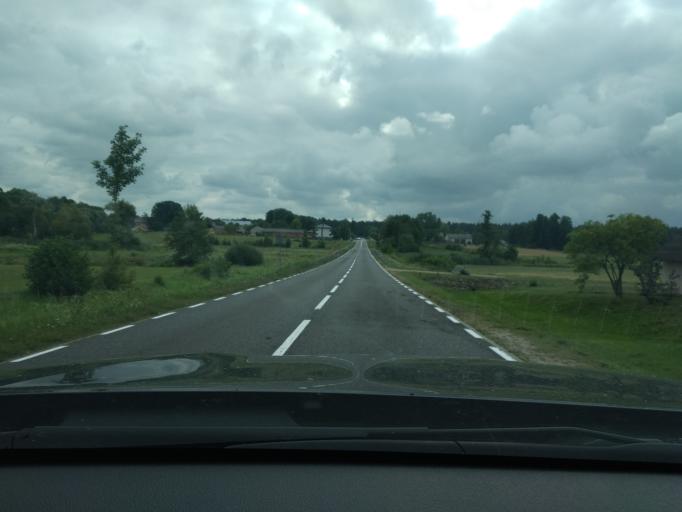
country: PL
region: Masovian Voivodeship
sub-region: Powiat pultuski
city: Obryte
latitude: 52.6493
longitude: 21.2465
